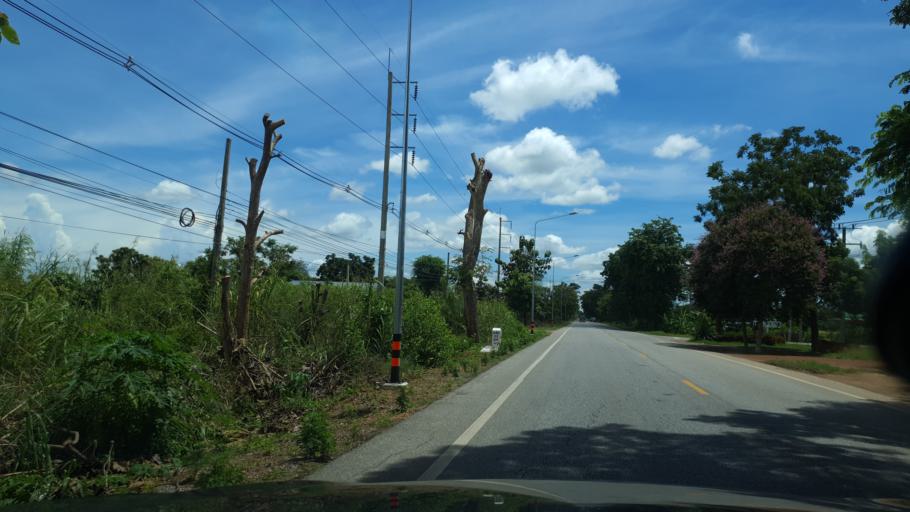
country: TH
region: Sukhothai
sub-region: Amphoe Si Satchanalai
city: Si Satchanalai
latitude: 17.4660
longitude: 99.7771
